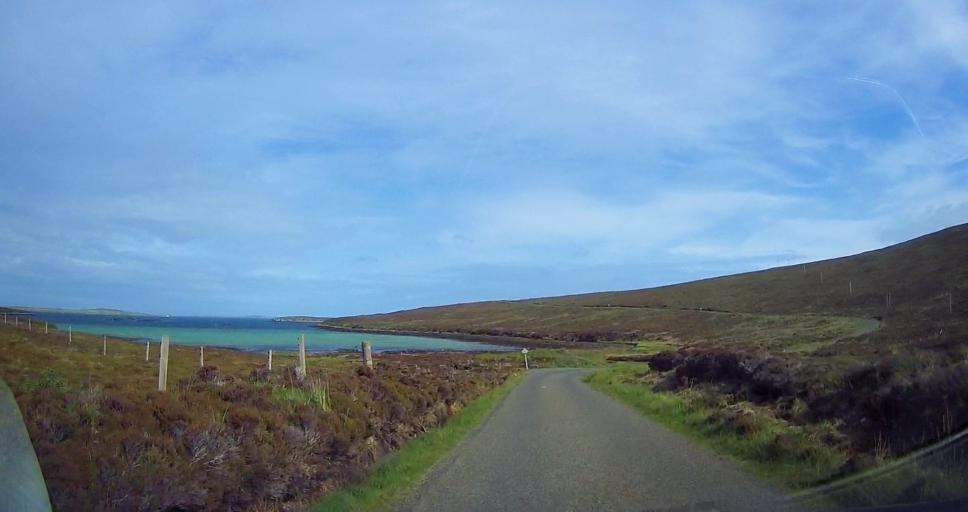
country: GB
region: Scotland
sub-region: Orkney Islands
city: Stromness
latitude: 58.8711
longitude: -3.2333
